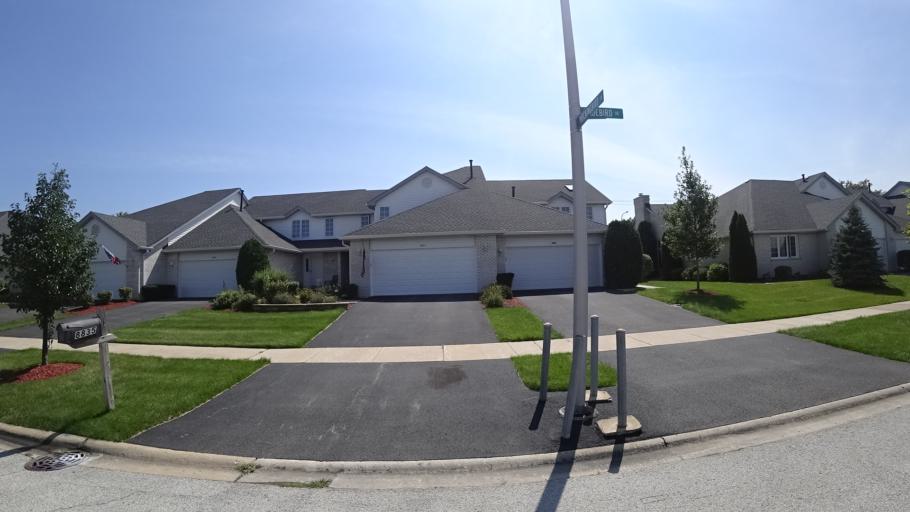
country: US
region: Illinois
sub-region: Cook County
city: Orland Hills
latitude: 41.5586
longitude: -87.8338
